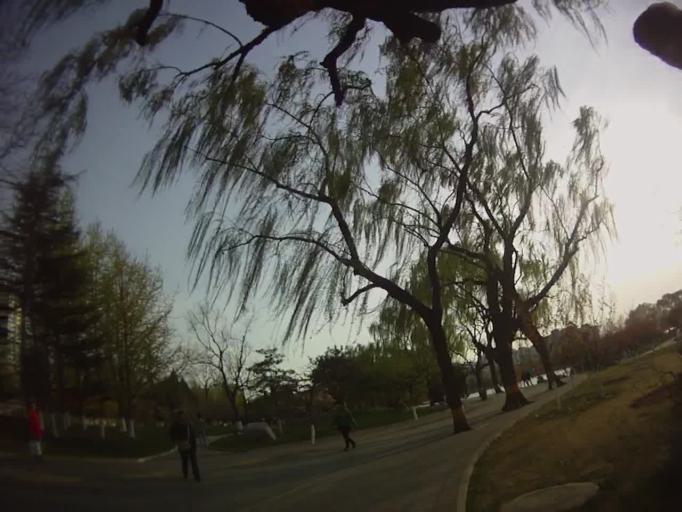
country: CN
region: Beijing
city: Longtan
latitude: 39.8767
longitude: 116.4384
